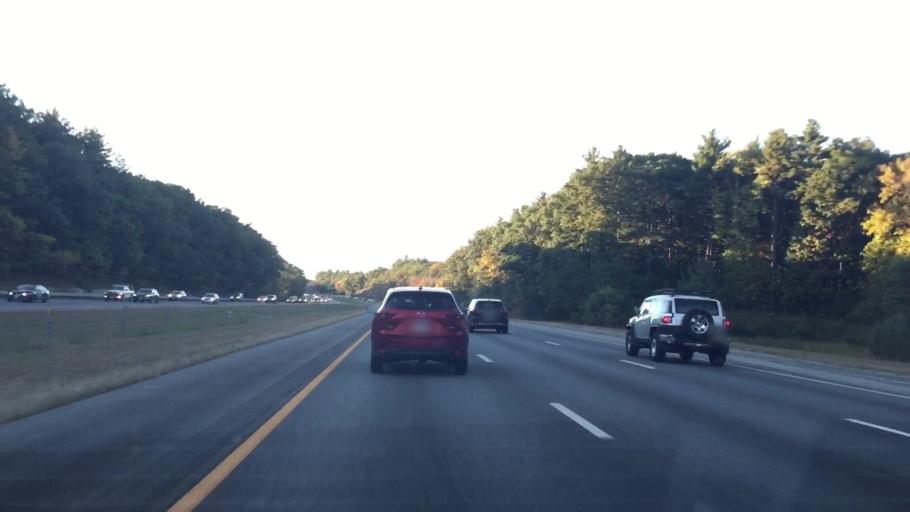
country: US
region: Massachusetts
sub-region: Middlesex County
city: Bedford
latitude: 42.5200
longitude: -71.2610
